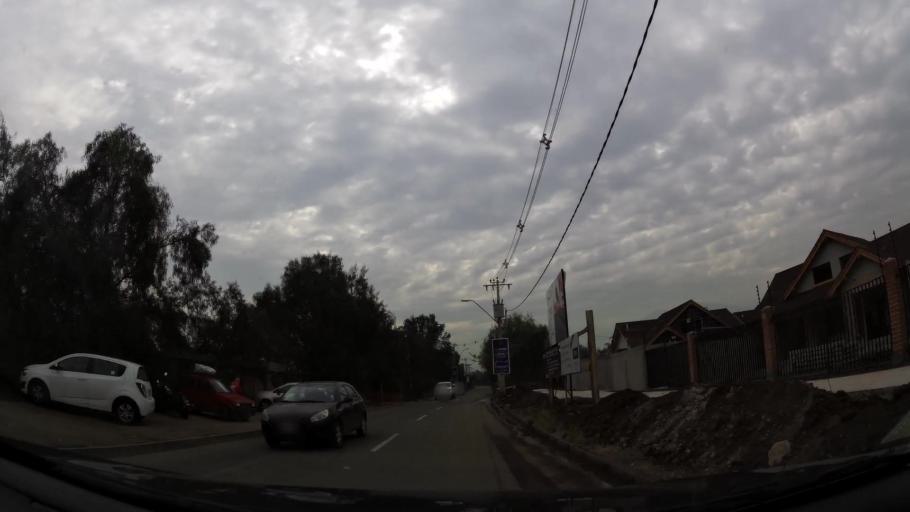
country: CL
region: Santiago Metropolitan
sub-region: Provincia de Chacabuco
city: Chicureo Abajo
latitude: -33.2161
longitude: -70.6632
